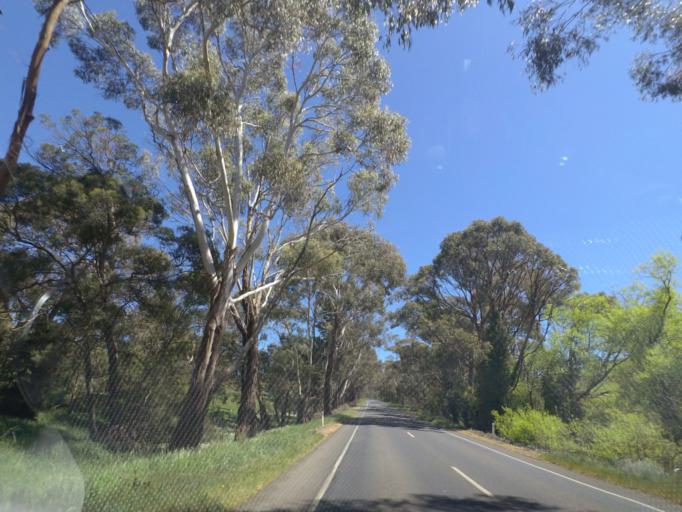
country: AU
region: Victoria
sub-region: Hume
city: Sunbury
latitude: -37.2960
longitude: 144.8020
